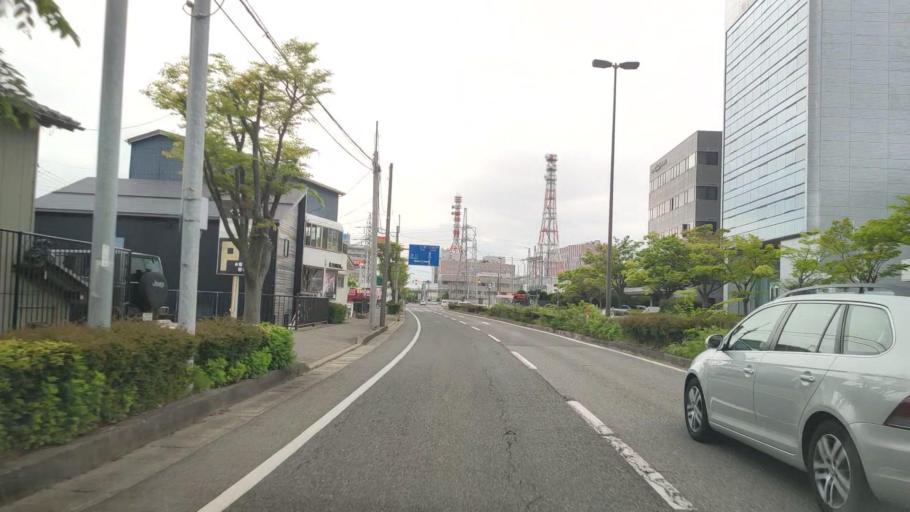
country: JP
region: Niigata
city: Niigata-shi
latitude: 37.8991
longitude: 139.0222
